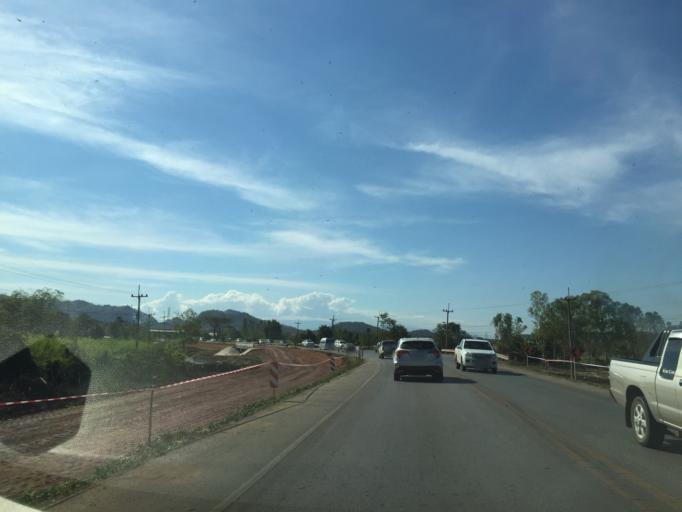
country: TH
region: Loei
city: Wang Saphung
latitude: 17.2992
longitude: 101.8595
